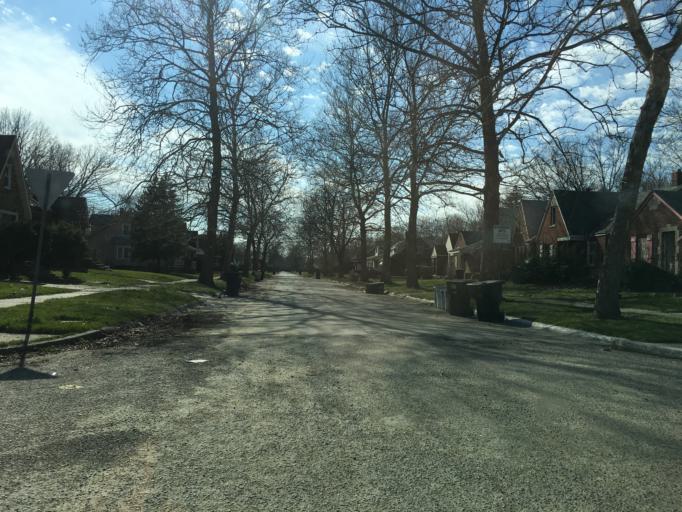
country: US
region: Michigan
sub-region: Macomb County
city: Eastpointe
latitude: 42.4280
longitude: -82.9677
